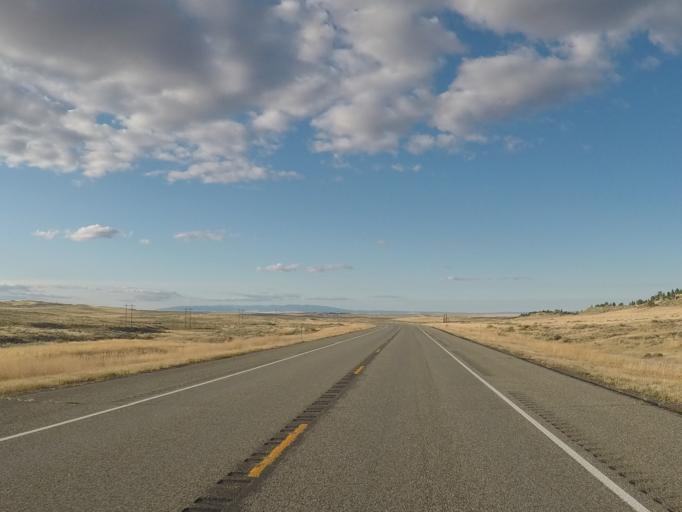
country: US
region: Montana
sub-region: Golden Valley County
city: Ryegate
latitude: 46.1624
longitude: -108.9001
